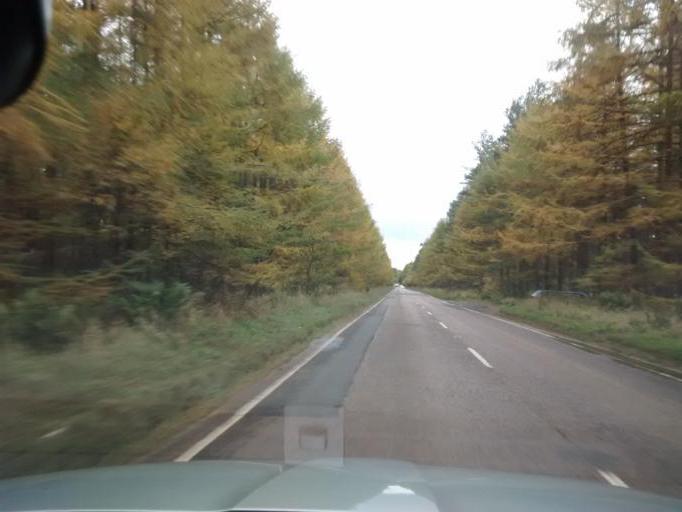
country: GB
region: Scotland
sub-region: Perth and Kinross
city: Blairgowrie
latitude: 56.5481
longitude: -3.3533
